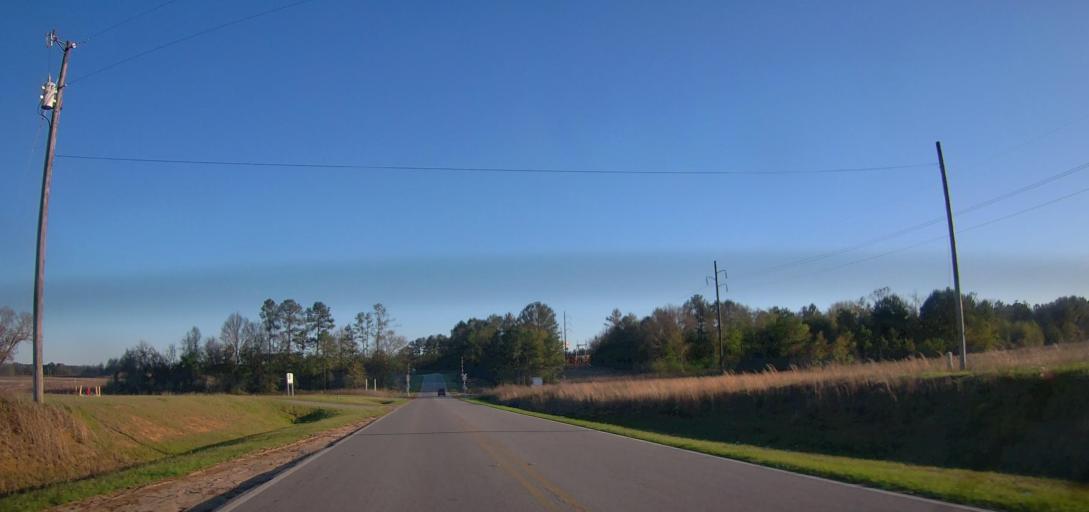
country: US
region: Georgia
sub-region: Wilkinson County
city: Gordon
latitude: 32.8952
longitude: -83.3014
